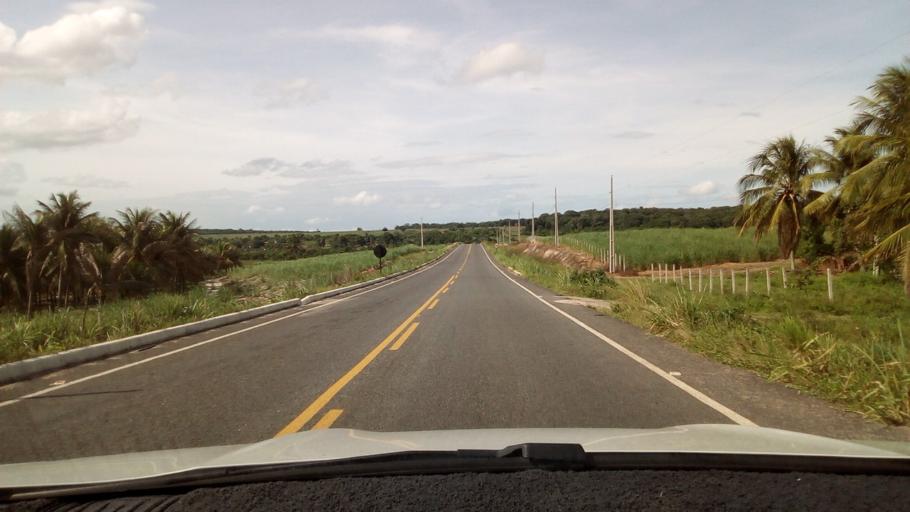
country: BR
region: Paraiba
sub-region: Santa Rita
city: Santa Rita
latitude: -7.0658
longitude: -34.9541
